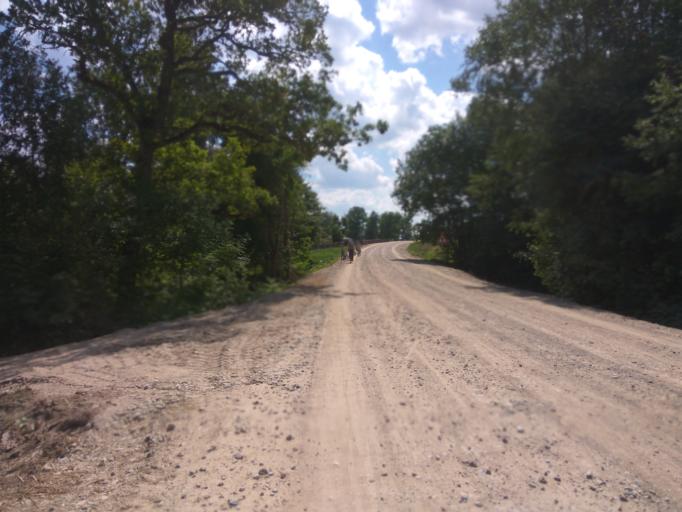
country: LV
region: Kuldigas Rajons
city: Kuldiga
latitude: 56.9060
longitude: 21.9647
